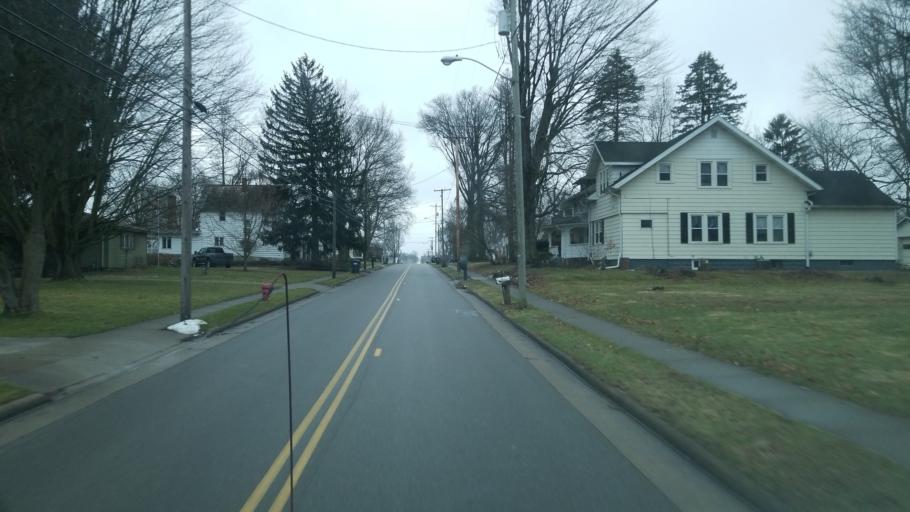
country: US
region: Ohio
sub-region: Wayne County
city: Smithville
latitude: 40.8575
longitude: -81.8617
